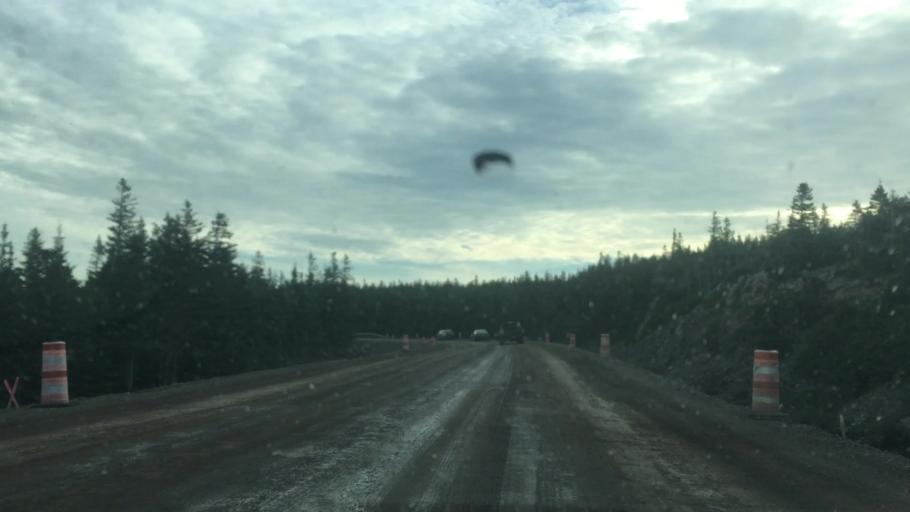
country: CA
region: Nova Scotia
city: Sydney Mines
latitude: 46.8079
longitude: -60.8431
